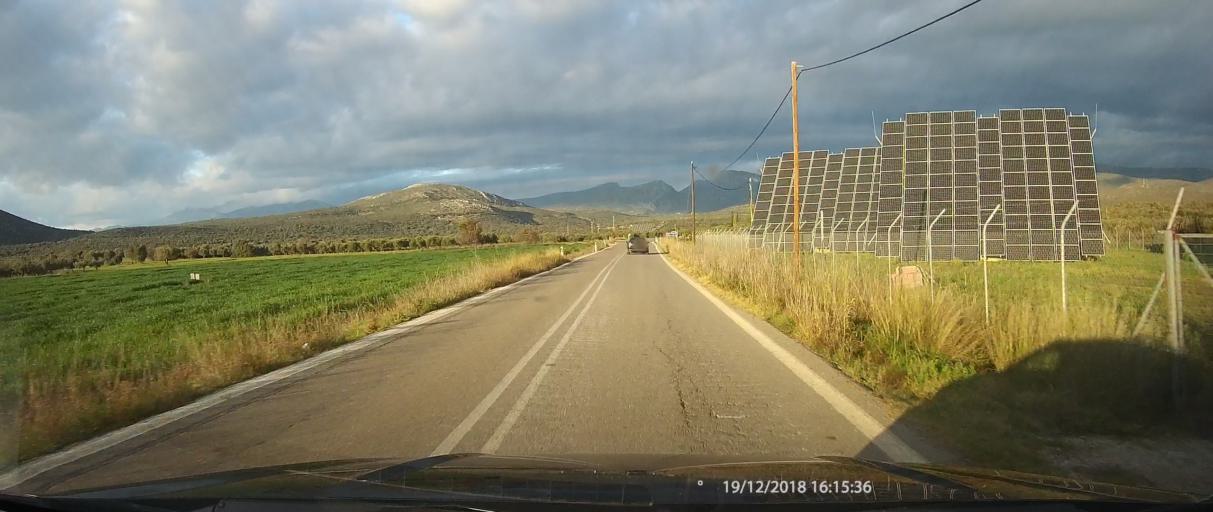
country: GR
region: Peloponnese
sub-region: Nomos Lakonias
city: Kato Glikovrisi
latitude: 36.8918
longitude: 22.8016
